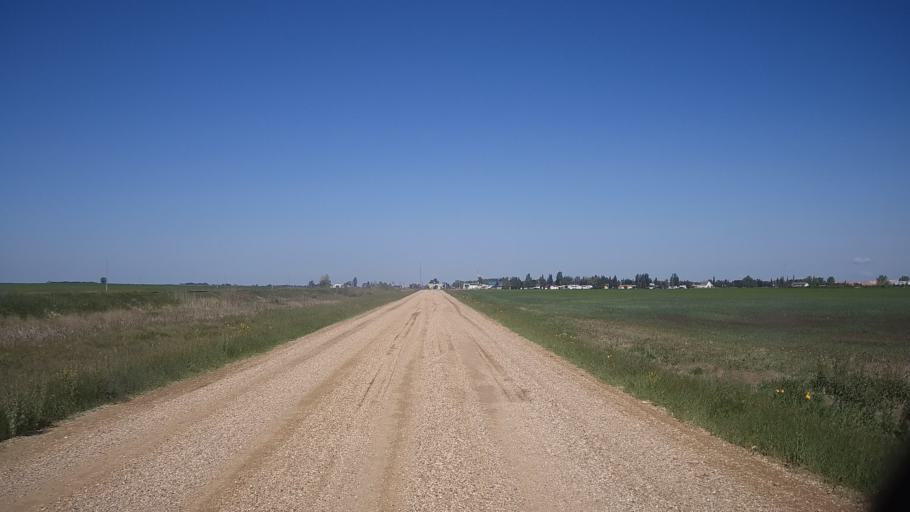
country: CA
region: Saskatchewan
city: Watrous
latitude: 51.8873
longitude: -106.0405
